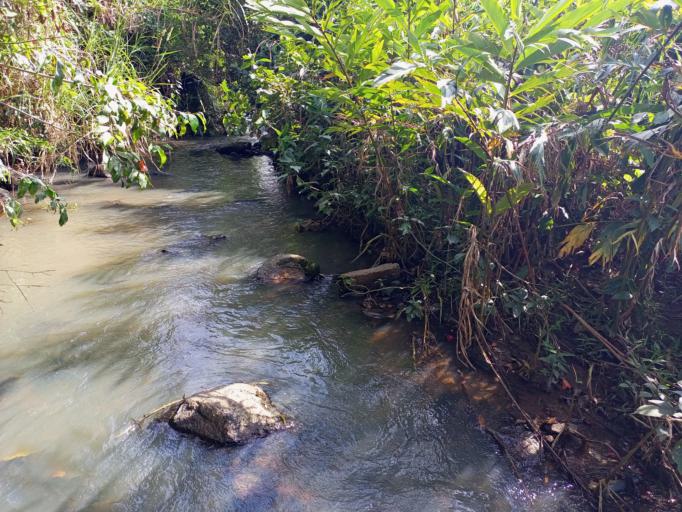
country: CD
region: Eastern Province
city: Bunia
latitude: 1.5366
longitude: 30.2960
